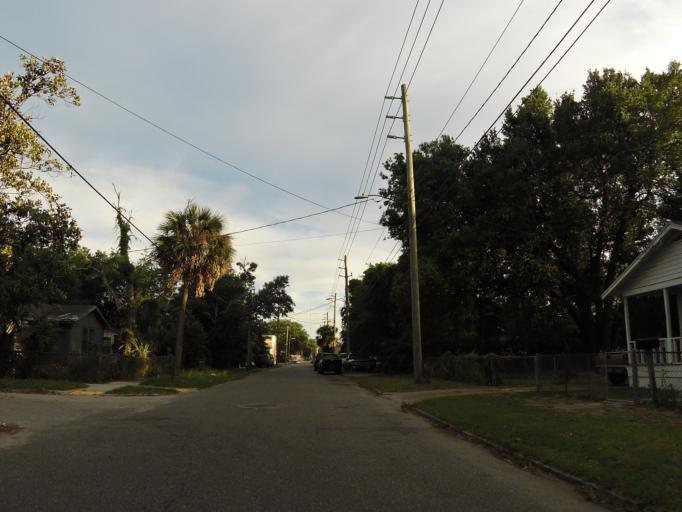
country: US
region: Florida
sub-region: Duval County
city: Jacksonville
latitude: 30.3472
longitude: -81.6432
